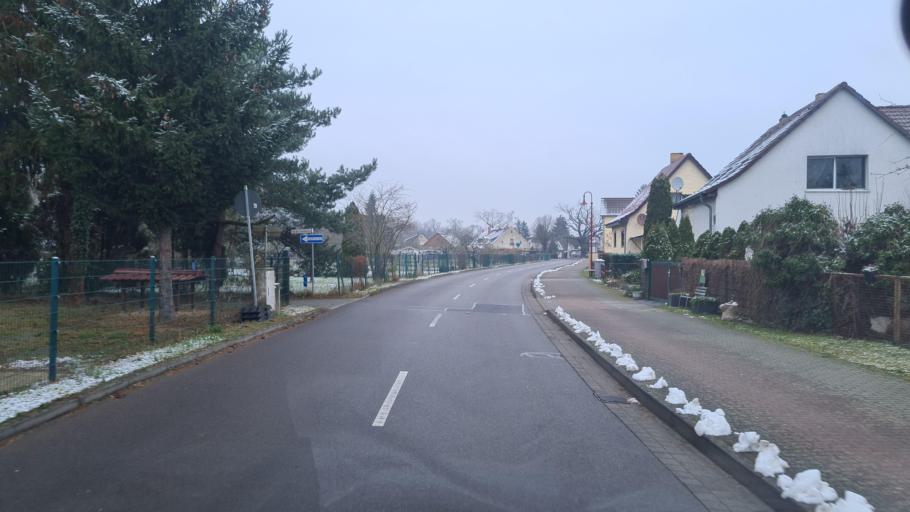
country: DE
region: Brandenburg
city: Storkow
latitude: 52.2526
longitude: 13.8943
